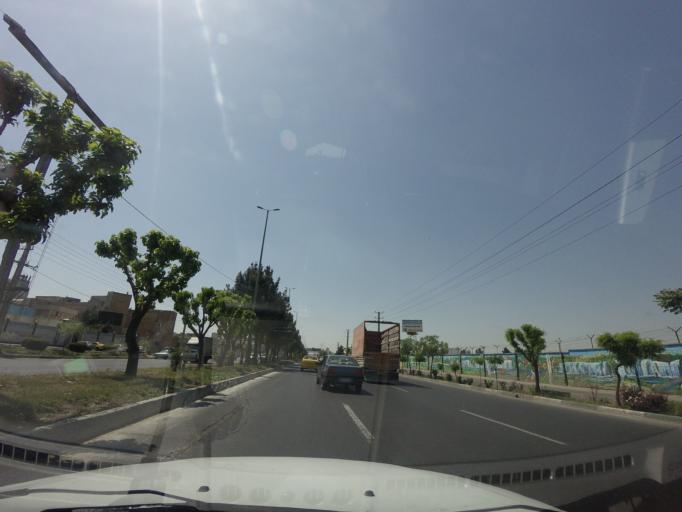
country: IR
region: Tehran
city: Eslamshahr
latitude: 35.6131
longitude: 51.3126
